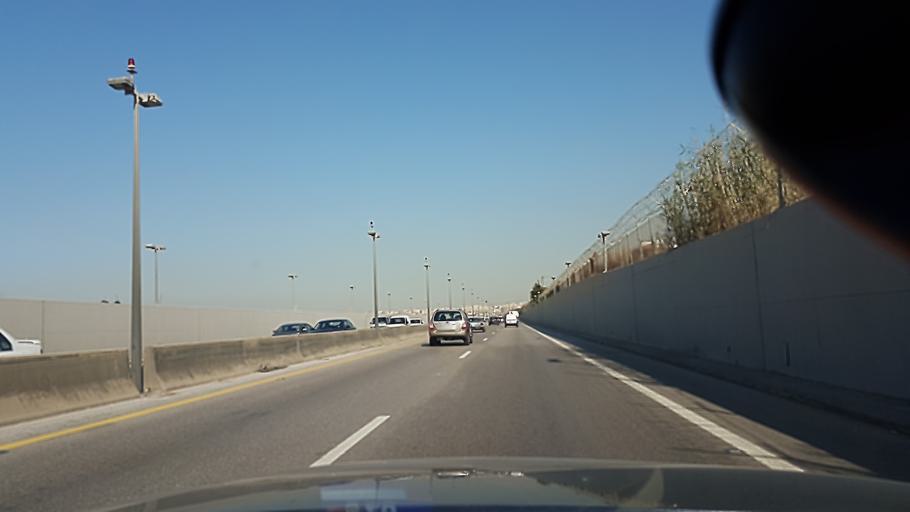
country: LB
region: Mont-Liban
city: Baabda
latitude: 33.8101
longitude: 35.4926
